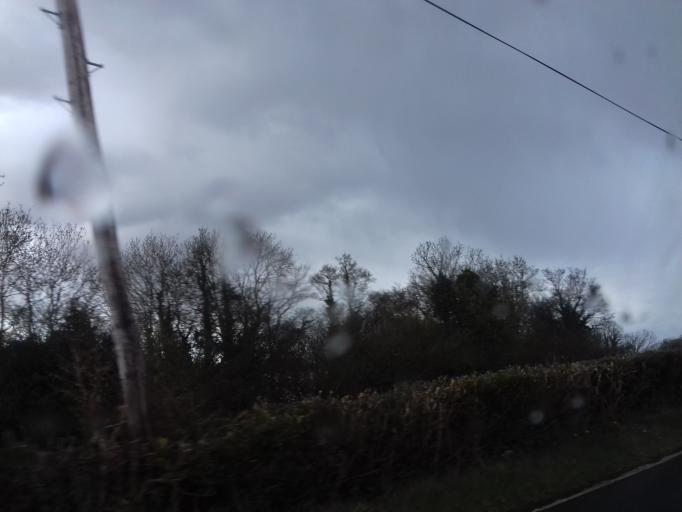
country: IE
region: Ulster
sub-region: County Donegal
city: Ballyshannon
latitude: 54.4734
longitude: -7.9486
